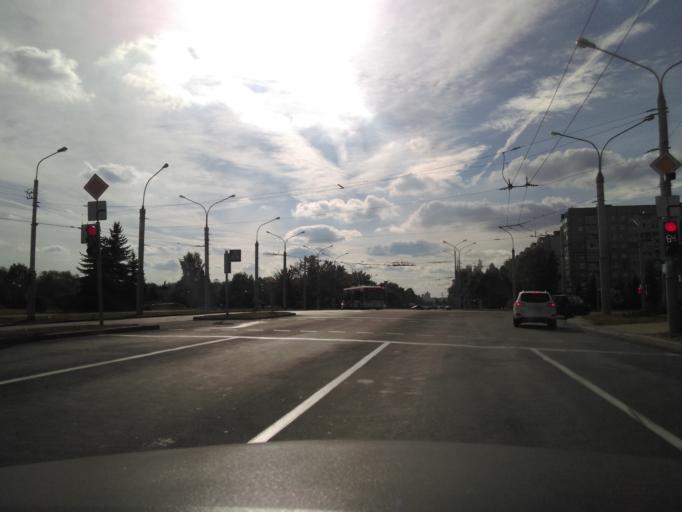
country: BY
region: Minsk
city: Minsk
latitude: 53.8527
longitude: 27.6152
